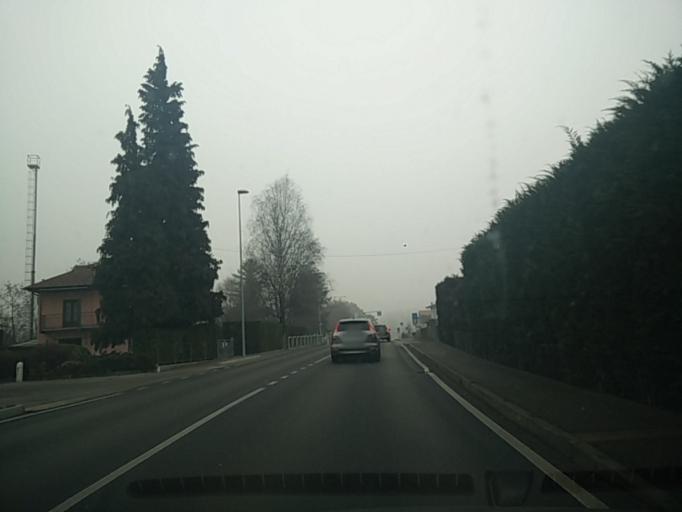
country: IT
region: Veneto
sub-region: Provincia di Belluno
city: Feltre
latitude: 46.0213
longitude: 11.9018
